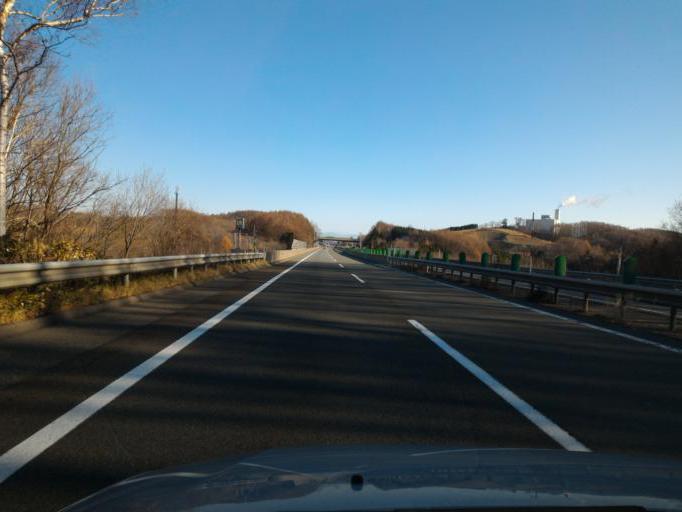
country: JP
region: Hokkaido
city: Iwamizawa
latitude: 43.1886
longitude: 141.7914
